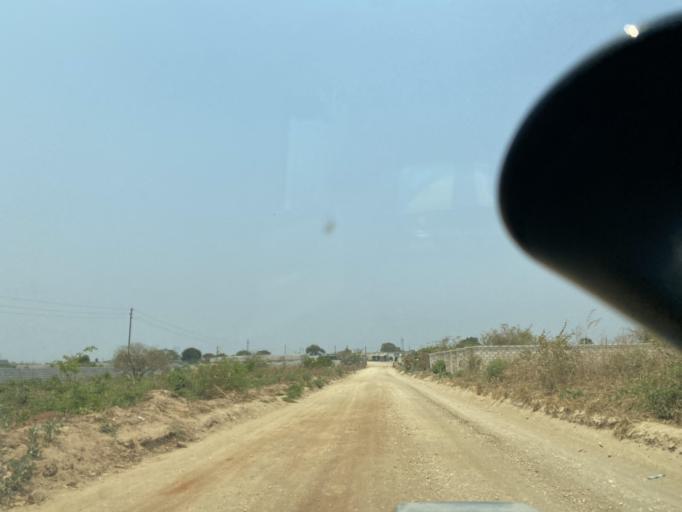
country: ZM
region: Lusaka
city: Lusaka
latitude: -15.5404
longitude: 28.3512
